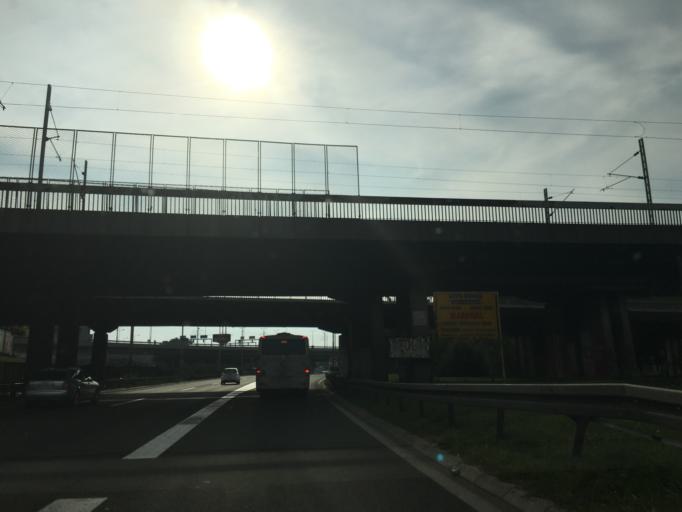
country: RS
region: Central Serbia
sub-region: Belgrade
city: Vracar
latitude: 44.7930
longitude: 20.4645
